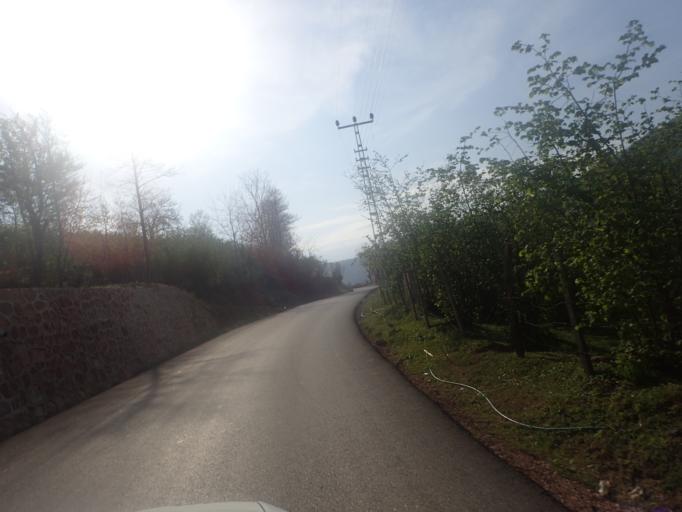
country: TR
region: Ordu
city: Camas
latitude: 40.8853
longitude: 37.4931
